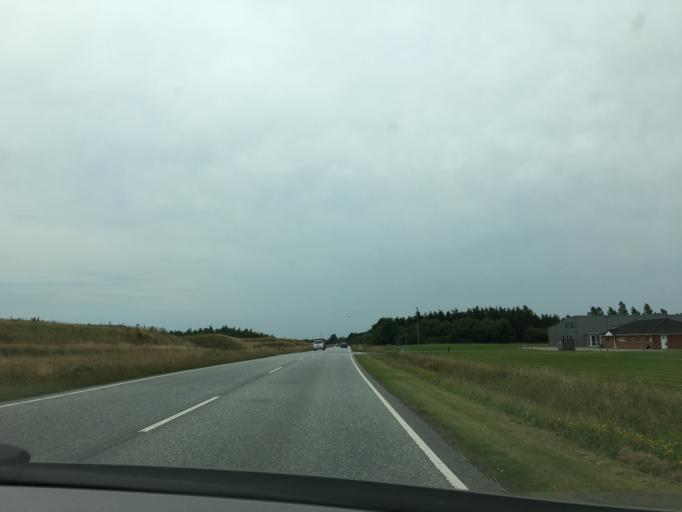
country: DK
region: Central Jutland
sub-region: Ringkobing-Skjern Kommune
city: Ringkobing
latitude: 56.0938
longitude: 8.2774
